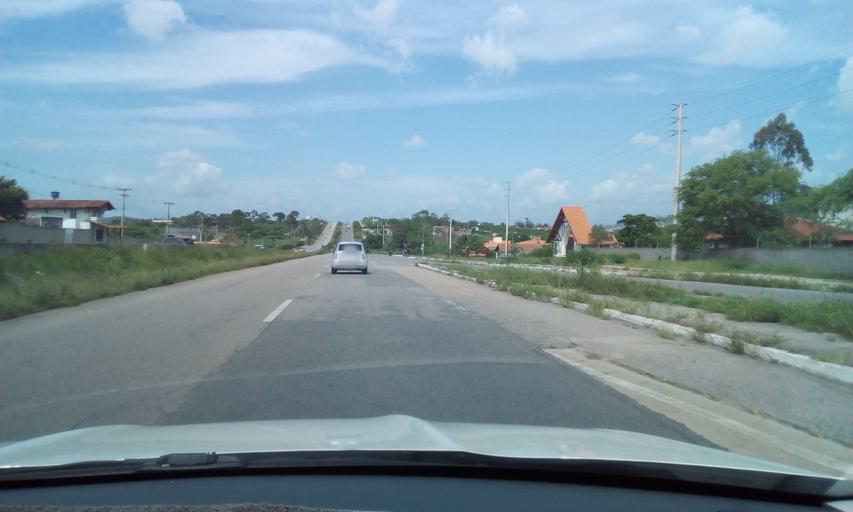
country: BR
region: Pernambuco
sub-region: Gravata
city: Gravata
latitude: -8.2098
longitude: -35.6120
